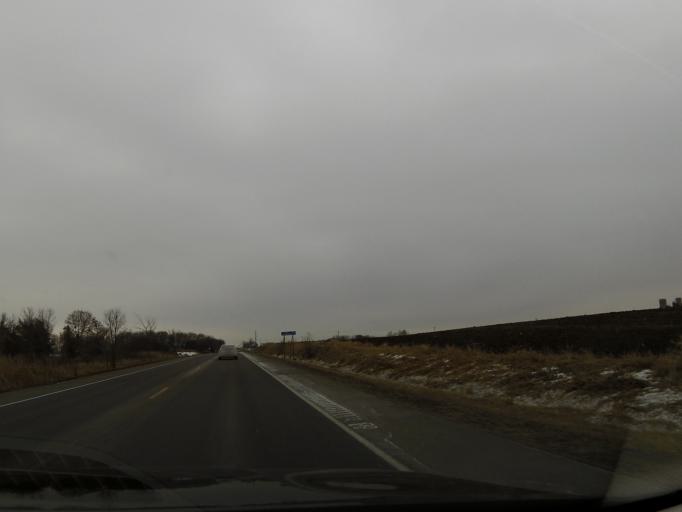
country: US
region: Minnesota
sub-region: Carver County
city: Cologne
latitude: 44.7678
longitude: -93.8325
